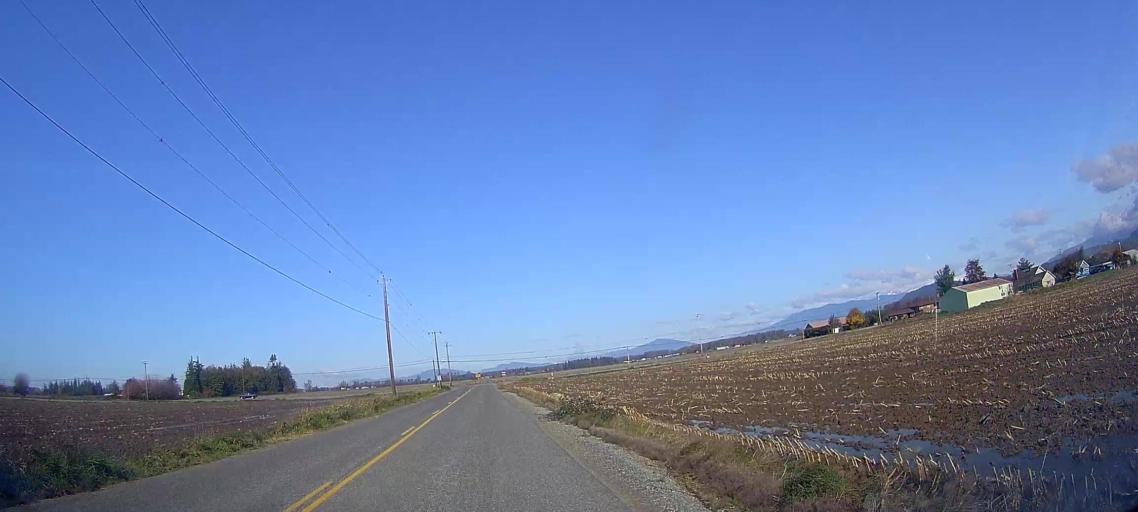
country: US
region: Washington
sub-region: Skagit County
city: Mount Vernon
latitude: 48.3404
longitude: -122.3807
